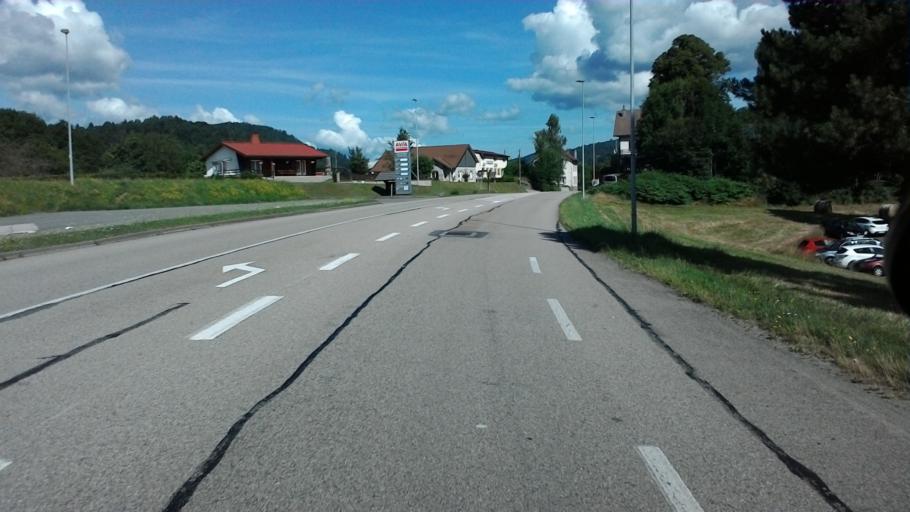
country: FR
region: Lorraine
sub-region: Departement des Vosges
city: Saint-Maurice-sur-Moselle
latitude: 47.8558
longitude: 6.8115
